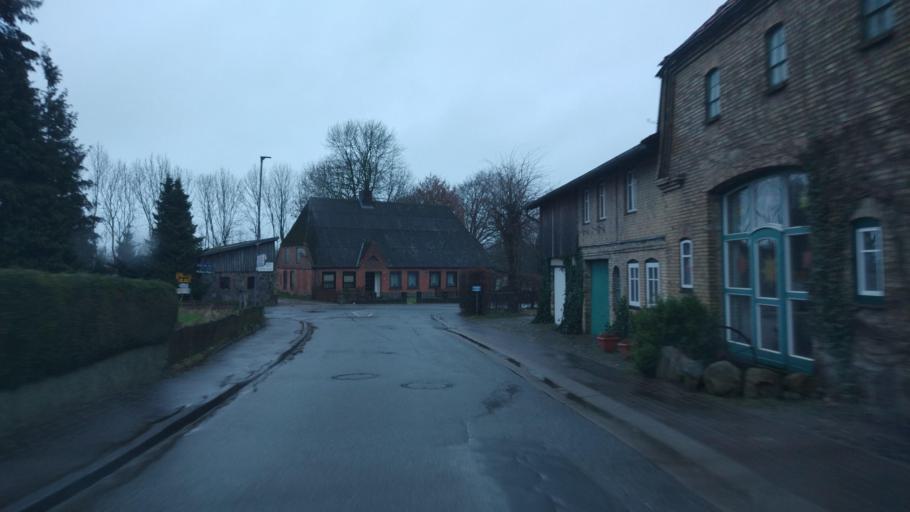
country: DE
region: Schleswig-Holstein
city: Guby
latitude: 54.4856
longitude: 9.6668
